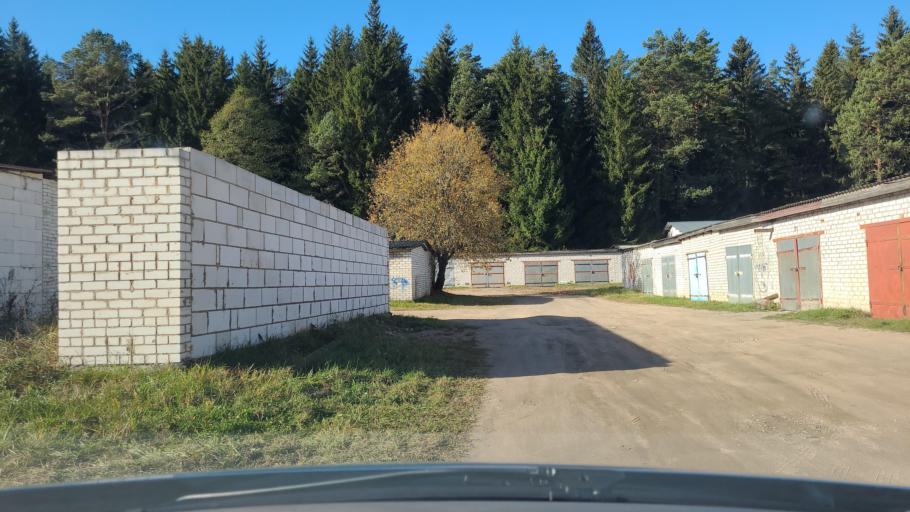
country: BY
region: Grodnenskaya
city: Astravyets
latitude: 54.6158
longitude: 25.9382
